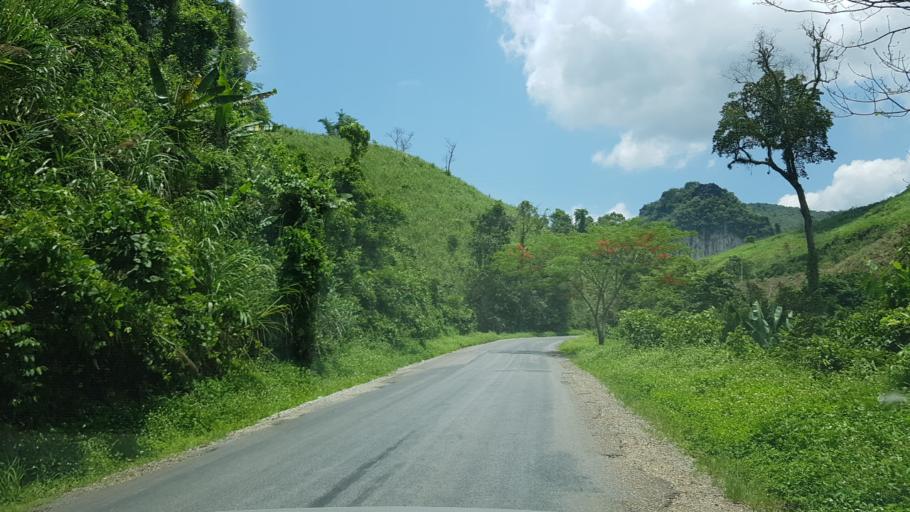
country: LA
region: Vientiane
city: Muang Kasi
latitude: 19.1381
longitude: 102.2907
